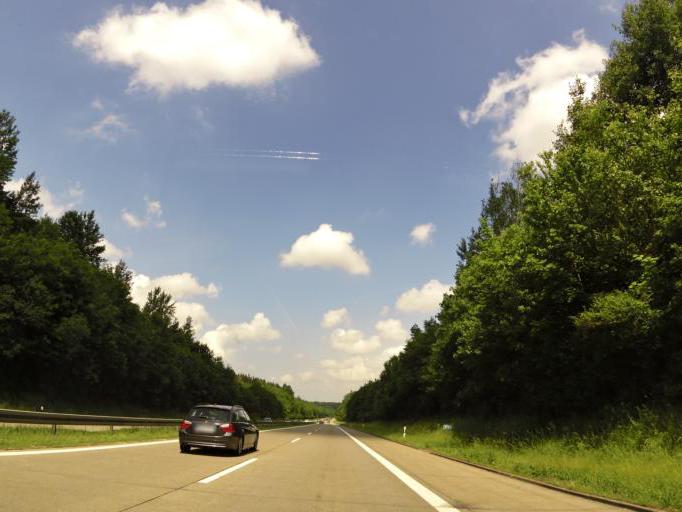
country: DE
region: Baden-Wuerttemberg
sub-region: Regierungsbezirk Stuttgart
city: Lauchheim
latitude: 48.7865
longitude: 10.2129
